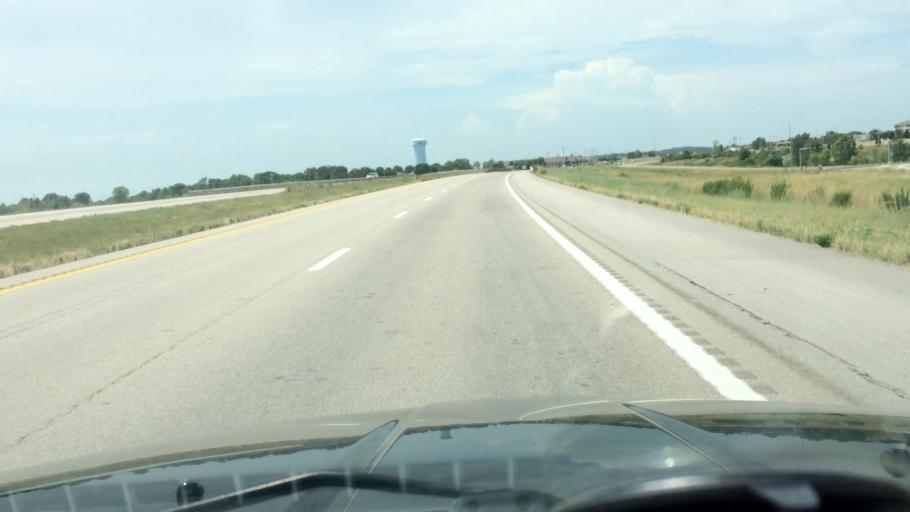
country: US
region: Missouri
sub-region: Polk County
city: Bolivar
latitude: 37.5916
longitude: -93.4303
